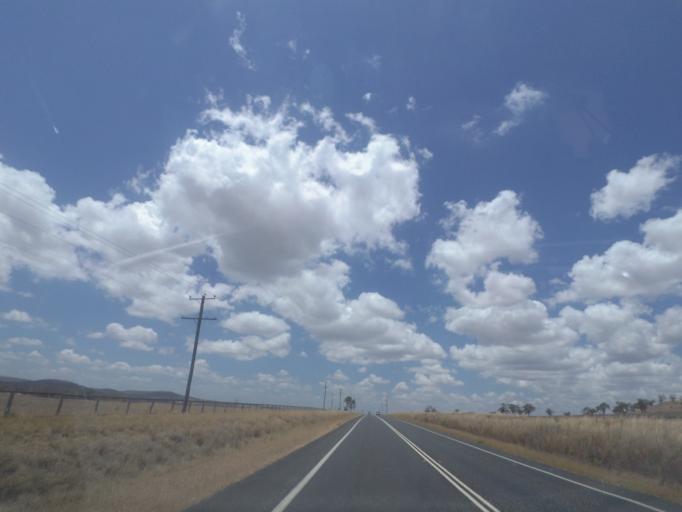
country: AU
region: Queensland
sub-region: Toowoomba
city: Top Camp
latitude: -27.7466
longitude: 151.9289
